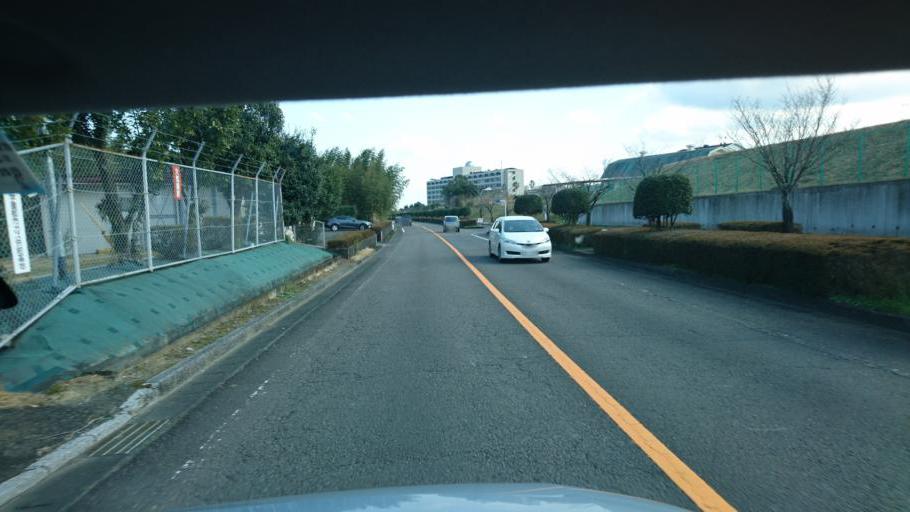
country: JP
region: Miyazaki
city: Miyazaki-shi
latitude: 31.8333
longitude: 131.4101
